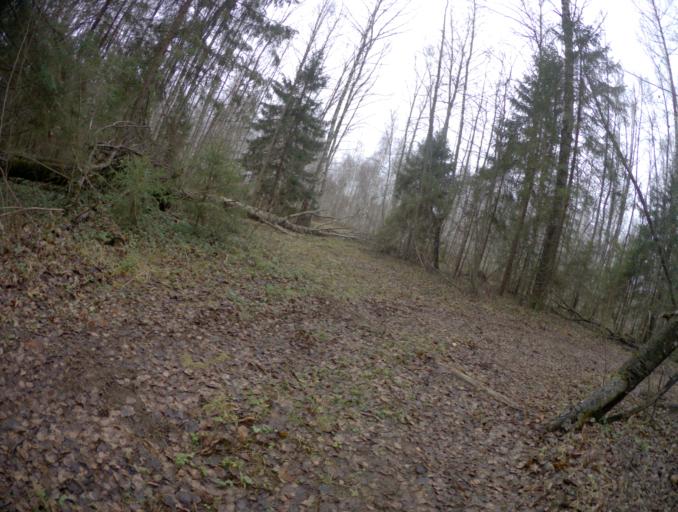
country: RU
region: Vladimir
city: Golovino
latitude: 56.0101
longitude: 40.5413
